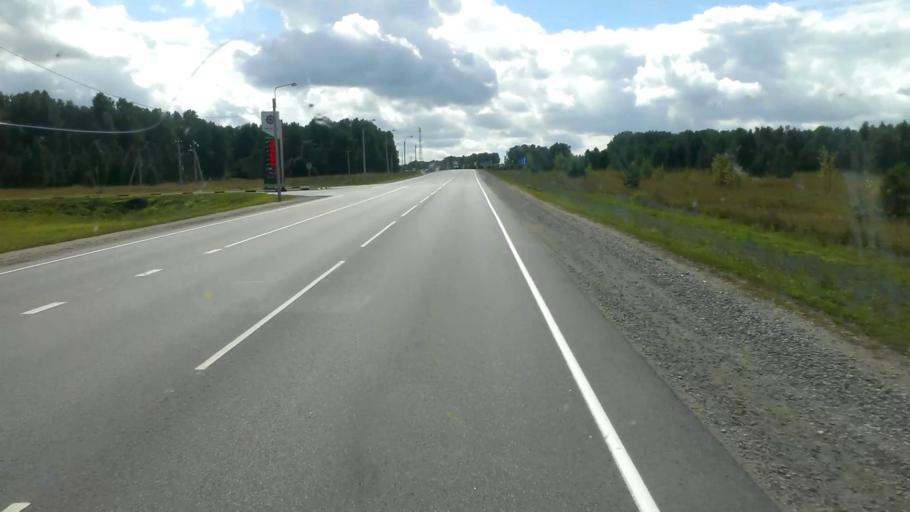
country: RU
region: Altai Krai
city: Troitskoye
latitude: 52.9747
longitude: 84.7470
